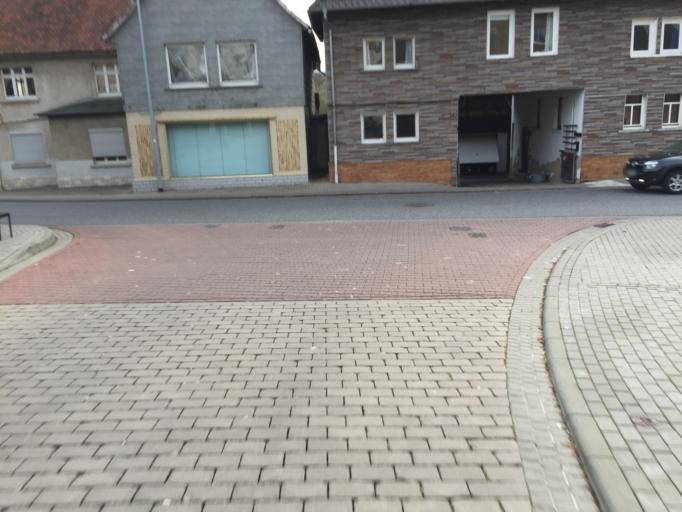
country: DE
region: Hesse
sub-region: Regierungsbezirk Giessen
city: Rabenau
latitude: 50.6754
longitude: 8.8606
